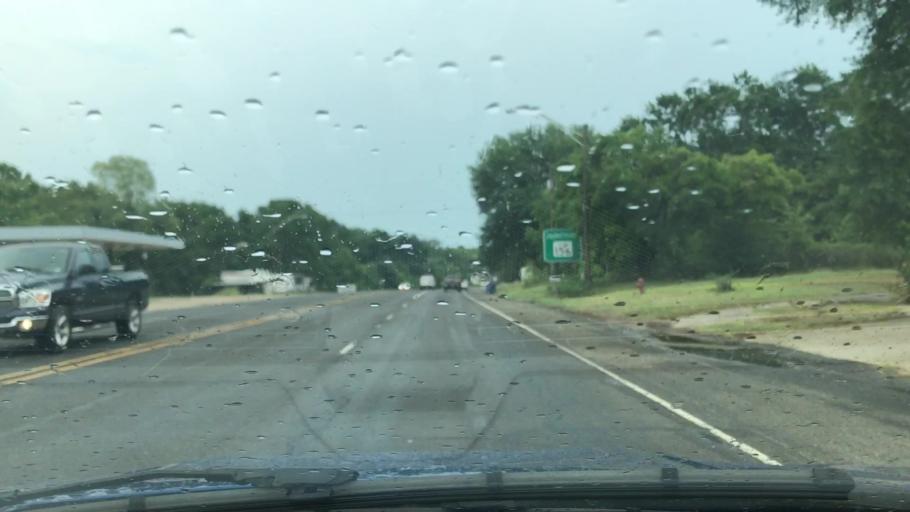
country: US
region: Texas
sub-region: Harrison County
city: Waskom
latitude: 32.4778
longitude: -94.0558
